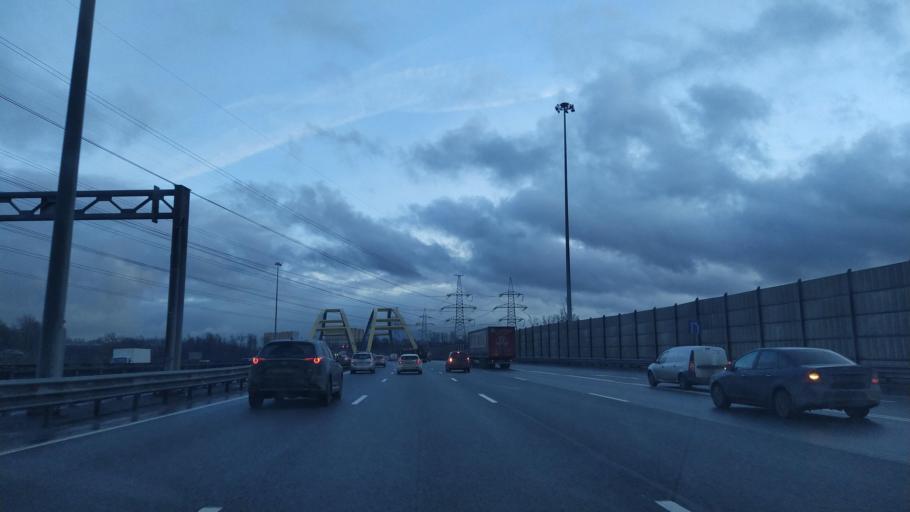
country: RU
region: St.-Petersburg
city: Krasnogvargeisky
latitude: 59.9877
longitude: 30.4874
